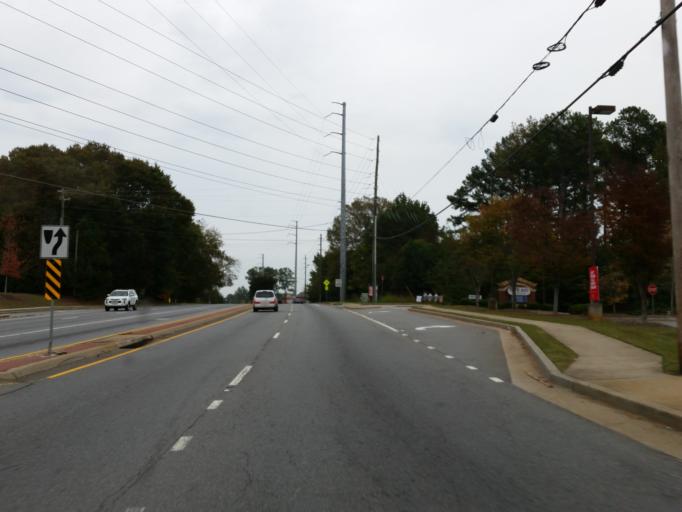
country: US
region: Georgia
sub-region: Cobb County
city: Marietta
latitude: 33.9959
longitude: -84.5076
